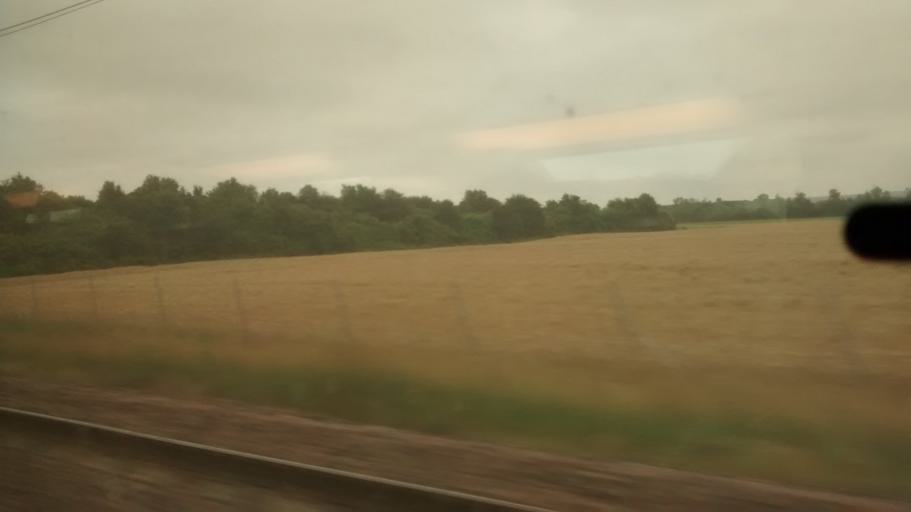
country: FR
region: Ile-de-France
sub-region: Departement de Seine-et-Marne
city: Marolles-sur-Seine
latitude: 48.3723
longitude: 3.0626
